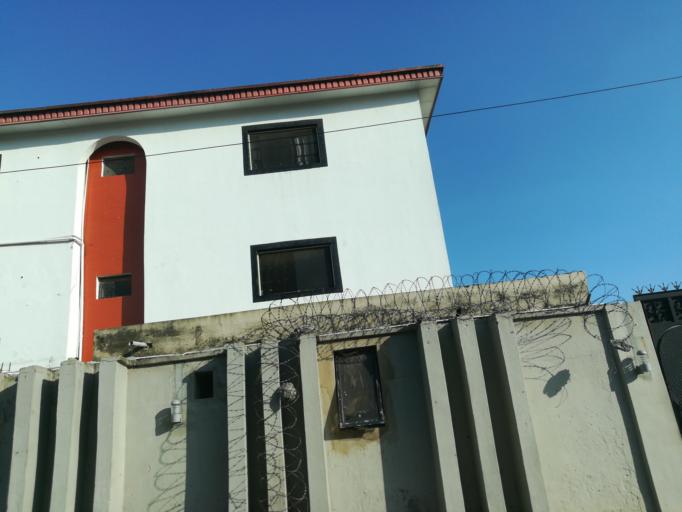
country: NG
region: Lagos
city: Ojota
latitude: 6.5835
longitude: 3.3673
